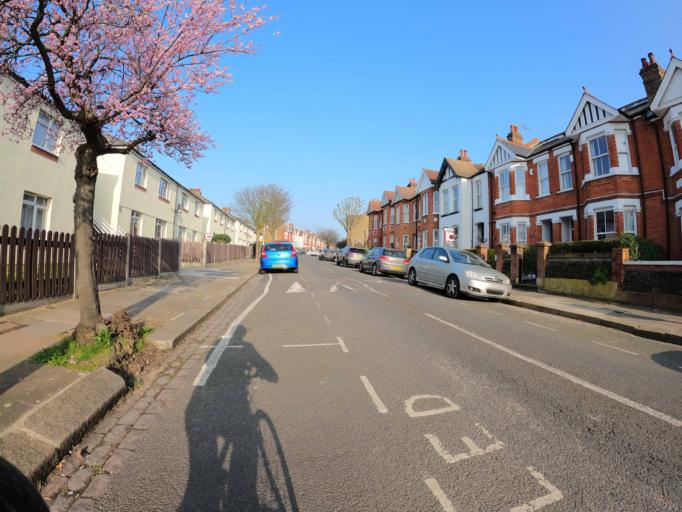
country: GB
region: England
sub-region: Greater London
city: Brentford
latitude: 51.4993
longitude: -0.3119
